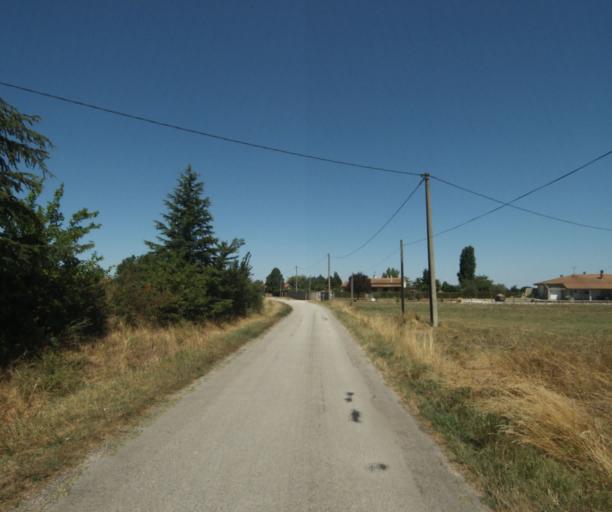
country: FR
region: Midi-Pyrenees
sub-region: Departement de la Haute-Garonne
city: Saint-Felix-Lauragais
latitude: 43.4477
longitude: 1.9372
